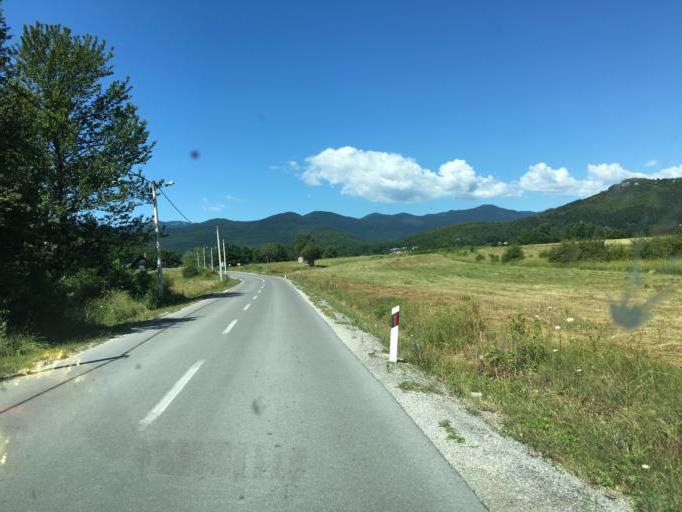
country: HR
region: Licko-Senjska
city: Gospic
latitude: 44.5615
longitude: 15.3173
